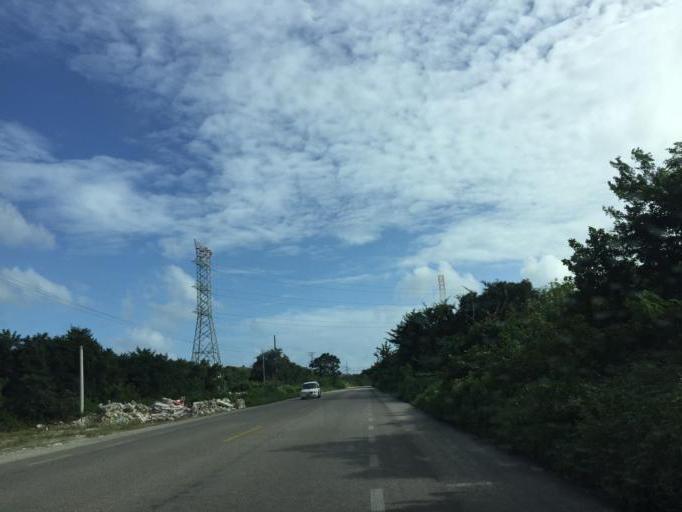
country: MX
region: Quintana Roo
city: Tulum
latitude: 20.2611
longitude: -87.4724
